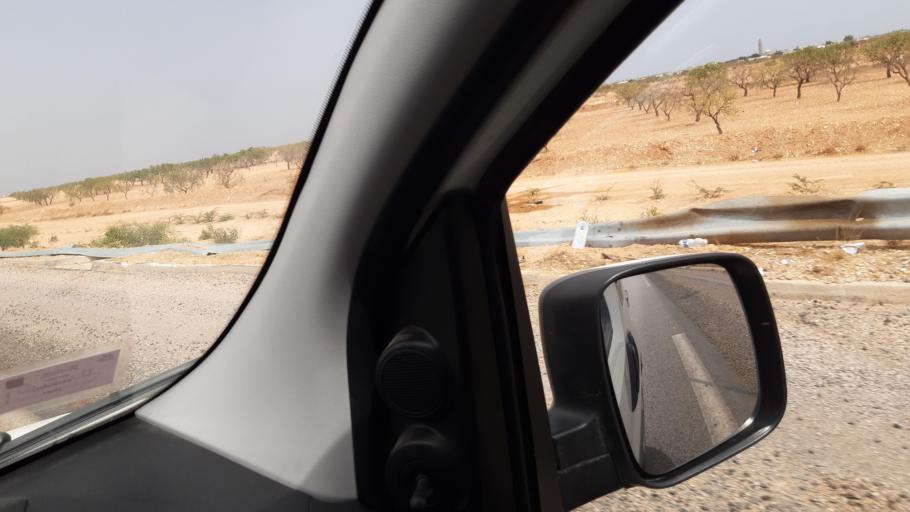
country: TN
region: Safaqis
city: Sfax
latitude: 34.8504
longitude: 10.6786
